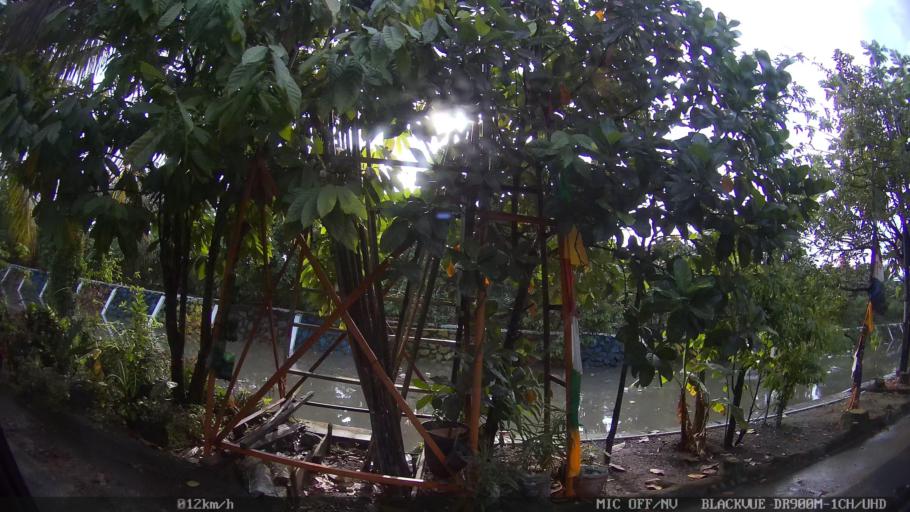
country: ID
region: Lampung
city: Kedaton
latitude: -5.3876
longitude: 105.3086
